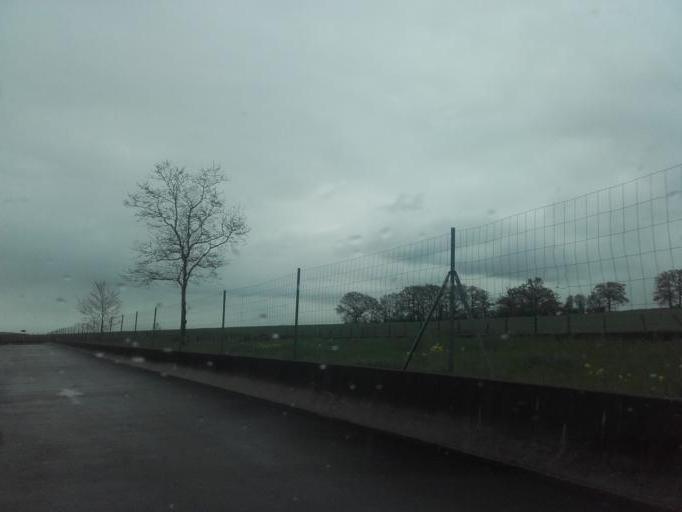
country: FR
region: Bourgogne
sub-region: Departement de l'Yonne
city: Avallon
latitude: 47.5016
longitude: 4.0374
